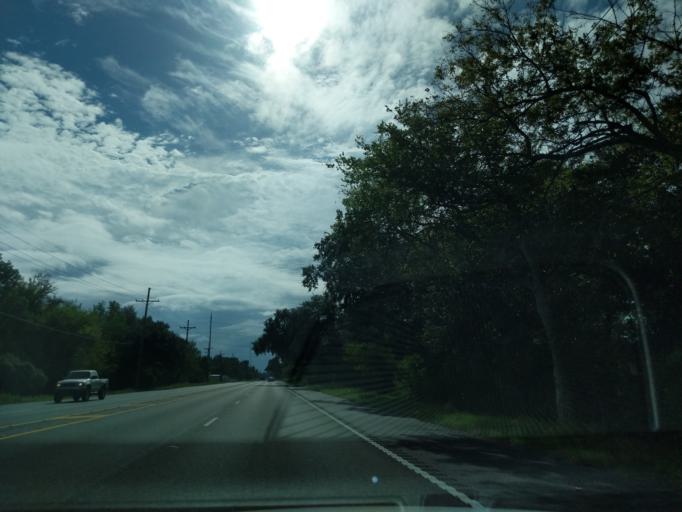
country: US
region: Louisiana
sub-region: Saint Bernard Parish
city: Meraux
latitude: 30.0536
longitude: -89.8782
